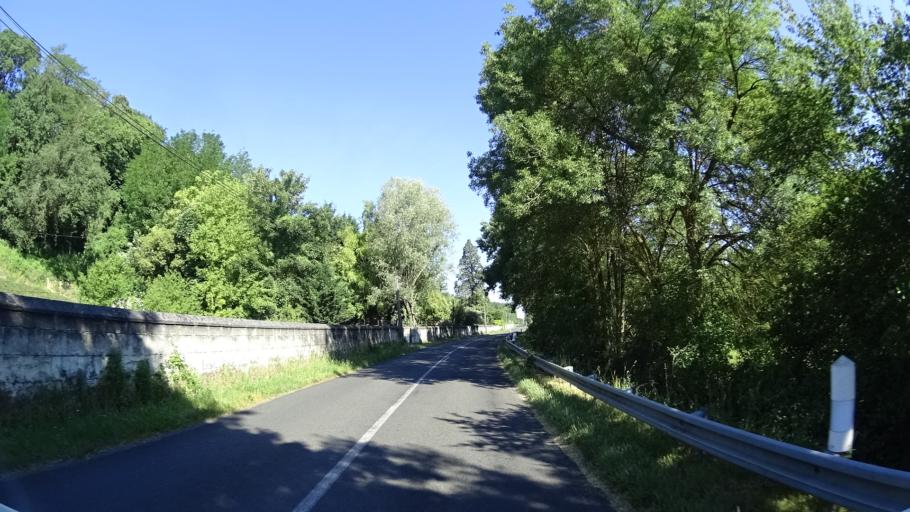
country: FR
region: Pays de la Loire
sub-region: Departement de Maine-et-Loire
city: Saint-Martin-de-la-Place
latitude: 47.2910
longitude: -0.1351
